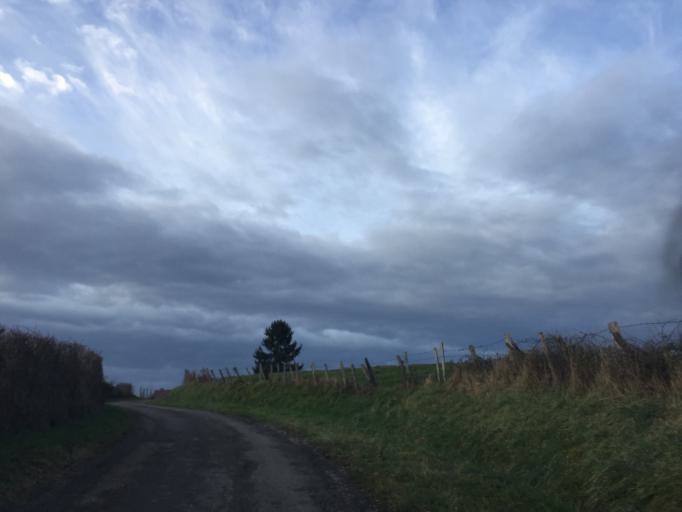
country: FR
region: Franche-Comte
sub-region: Departement du Jura
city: Arbois
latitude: 46.9376
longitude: 5.6874
